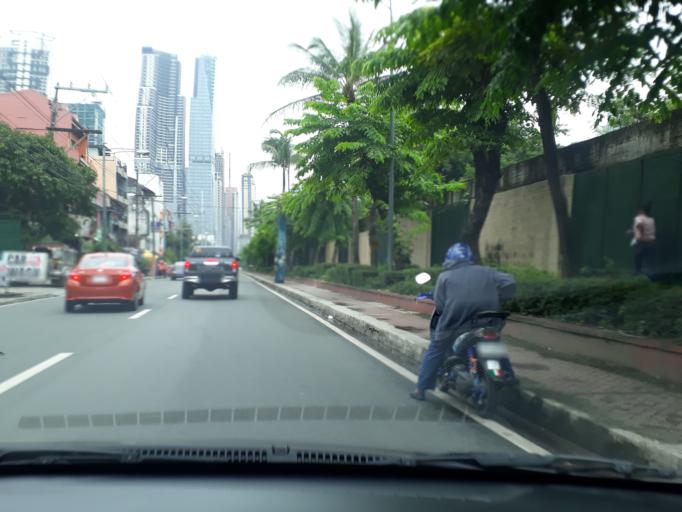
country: PH
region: Metro Manila
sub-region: Makati City
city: Makati City
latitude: 14.5678
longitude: 121.0205
